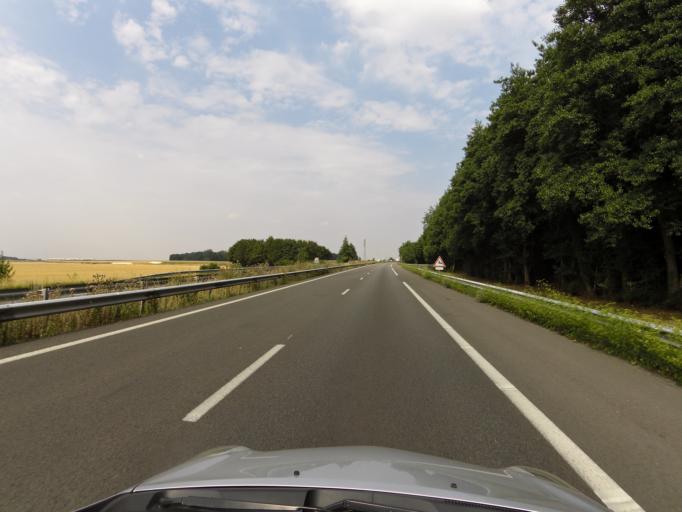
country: FR
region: Picardie
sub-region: Departement de l'Aisne
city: Holnon
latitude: 49.8715
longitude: 3.2417
